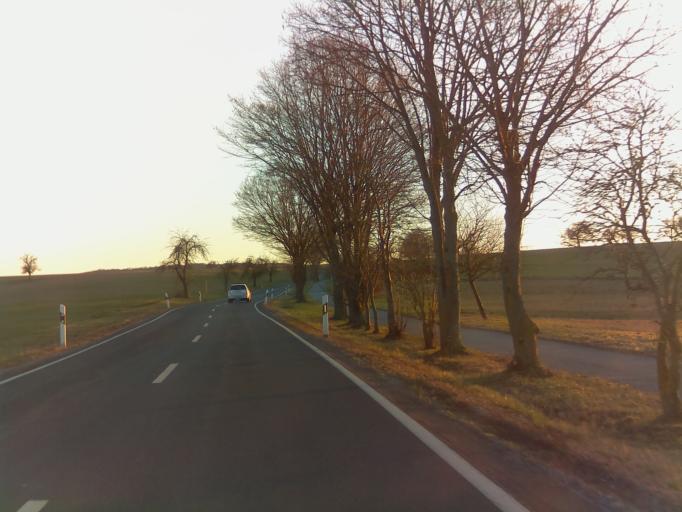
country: DE
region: Bavaria
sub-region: Regierungsbezirk Unterfranken
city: Geiselbach
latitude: 50.1170
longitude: 9.1997
